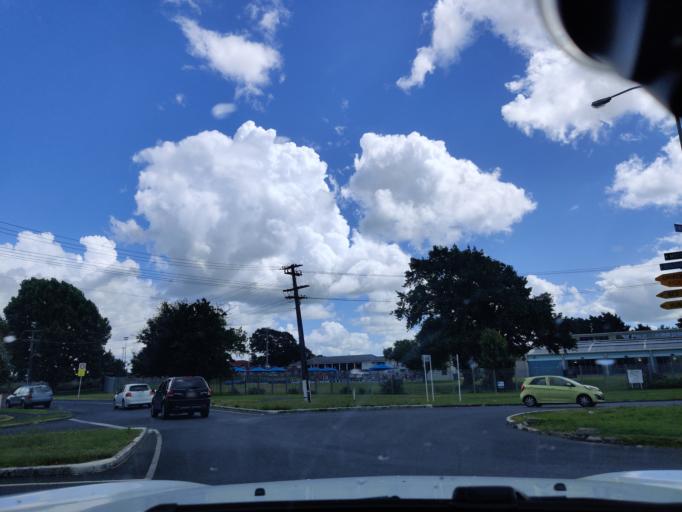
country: NZ
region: Auckland
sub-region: Auckland
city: Papakura
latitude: -37.0623
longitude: 174.9481
